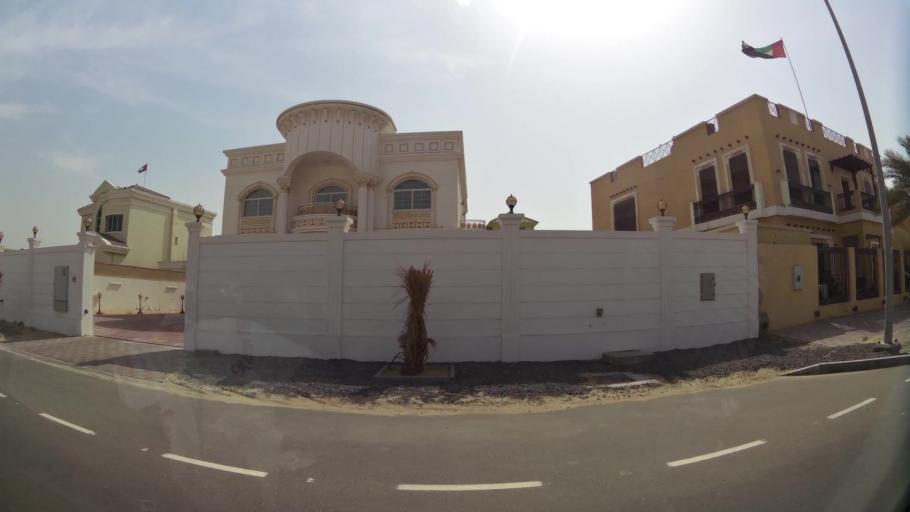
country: AE
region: Ash Shariqah
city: Sharjah
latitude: 25.2662
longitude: 55.4707
